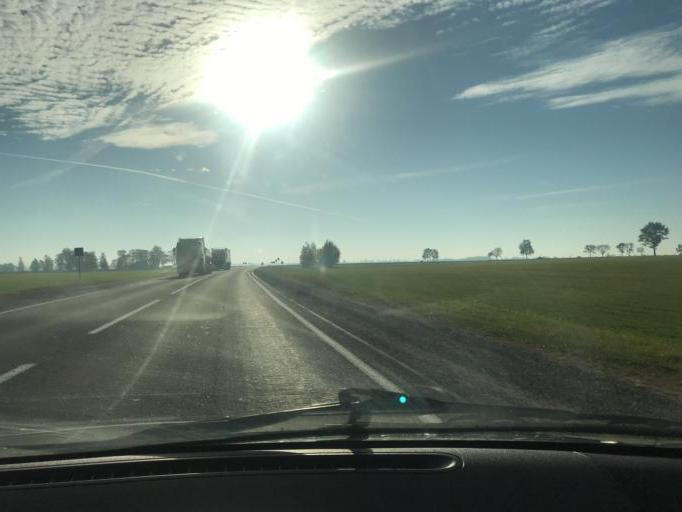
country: BY
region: Brest
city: Drahichyn
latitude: 52.2060
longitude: 25.2237
